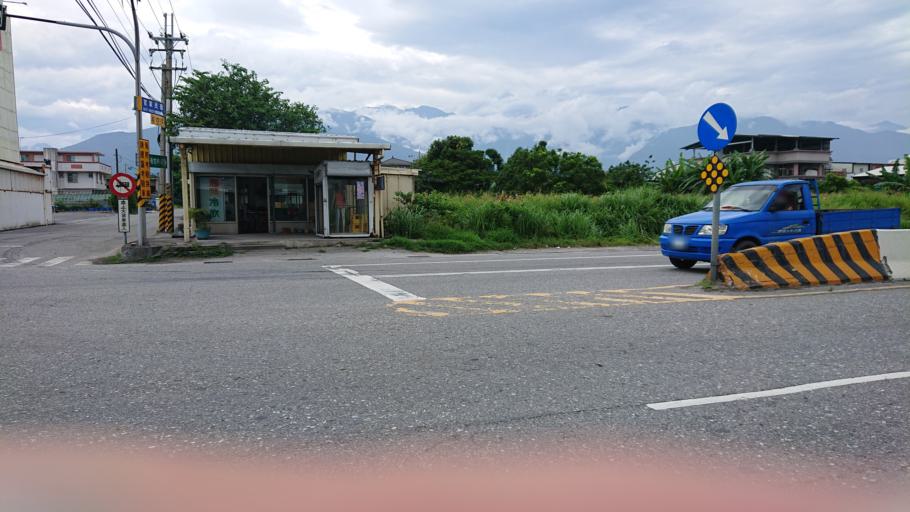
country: TW
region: Taiwan
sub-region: Hualien
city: Hualian
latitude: 23.9479
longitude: 121.5981
